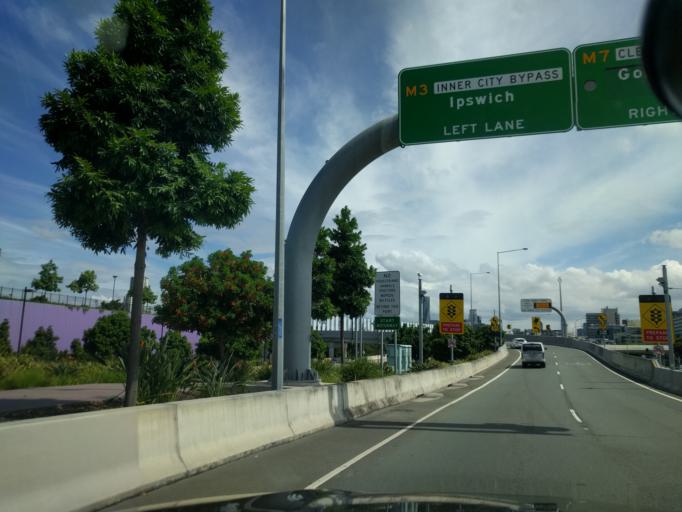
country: AU
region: Queensland
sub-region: Brisbane
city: Windsor
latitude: -27.4404
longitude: 153.0309
